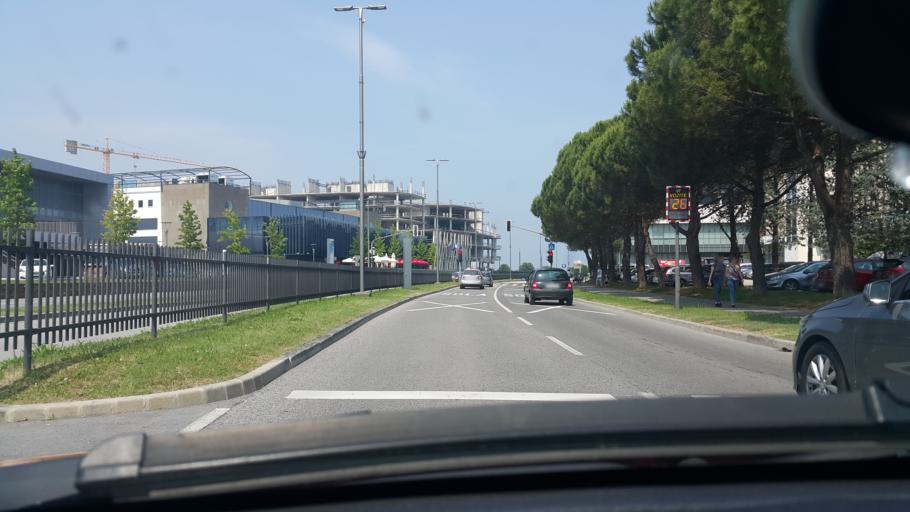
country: SI
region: Koper-Capodistria
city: Koper
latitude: 45.5435
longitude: 13.7290
